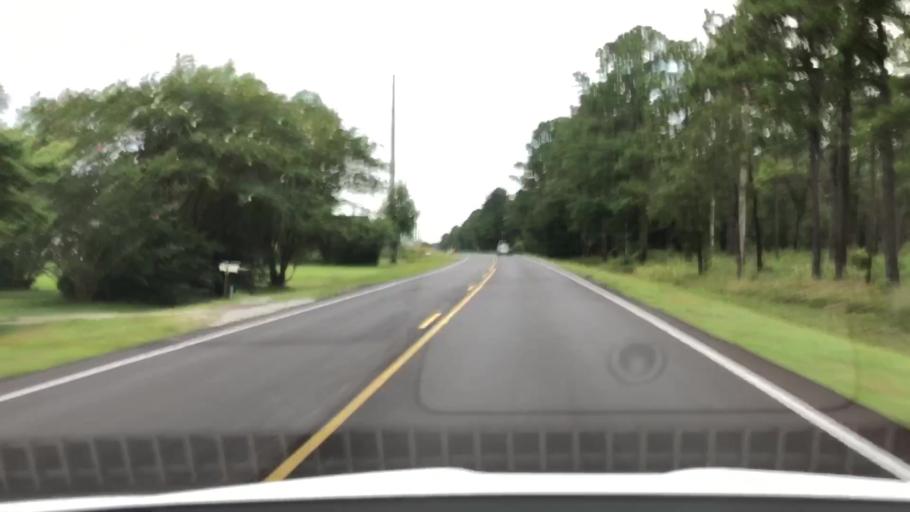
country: US
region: North Carolina
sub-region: Jones County
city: Maysville
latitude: 34.8301
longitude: -77.1594
